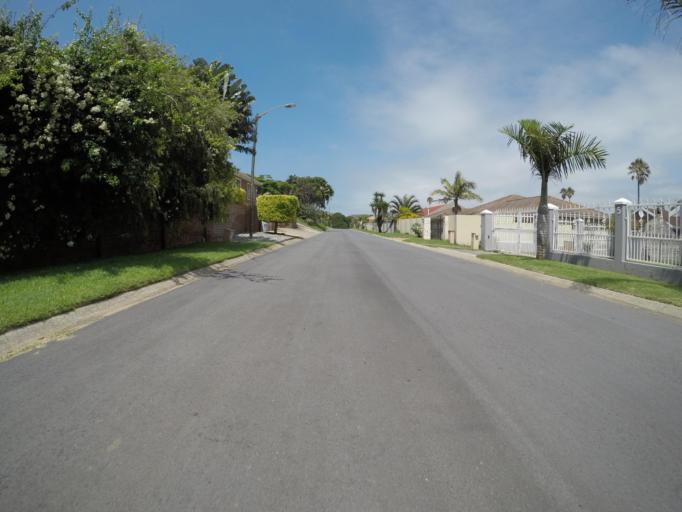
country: ZA
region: Eastern Cape
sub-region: Buffalo City Metropolitan Municipality
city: East London
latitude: -32.9460
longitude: 28.0210
